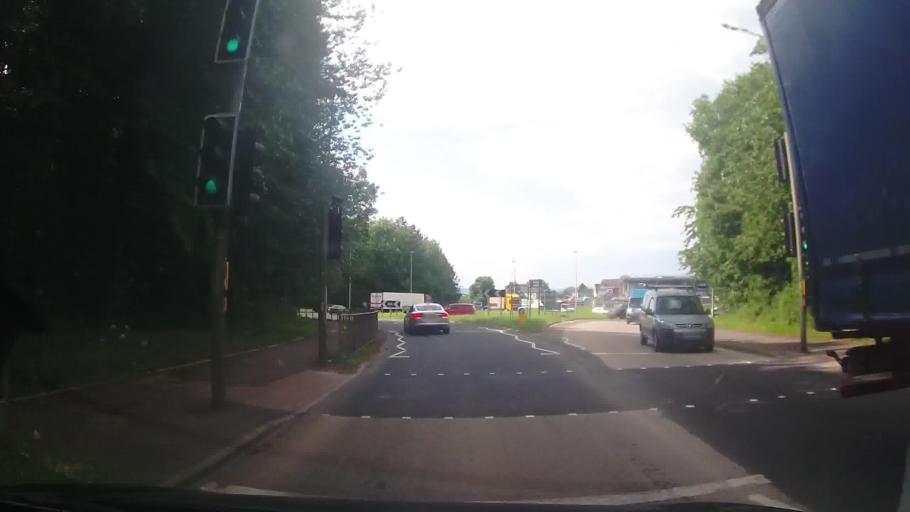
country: GB
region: England
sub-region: Shropshire
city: Ludlow
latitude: 52.3757
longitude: -2.7020
